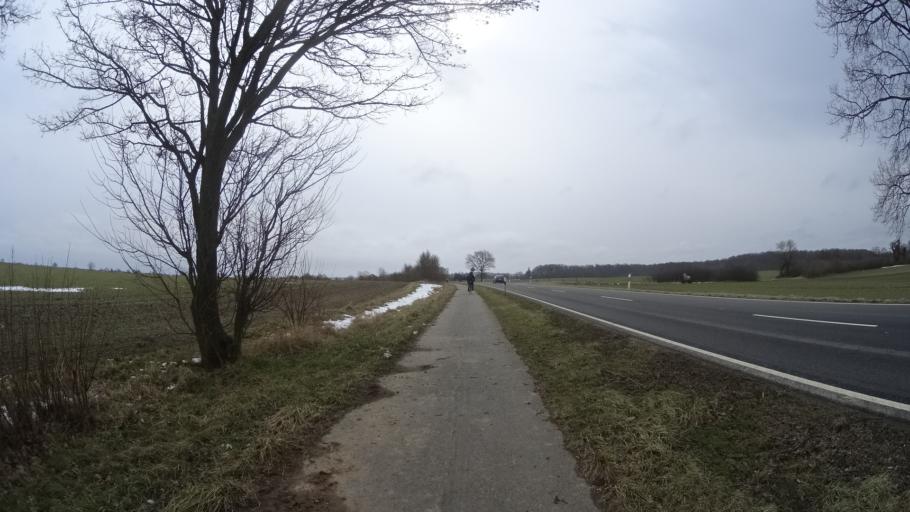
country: DE
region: Schleswig-Holstein
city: Hohenfelde
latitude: 54.3655
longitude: 10.5130
